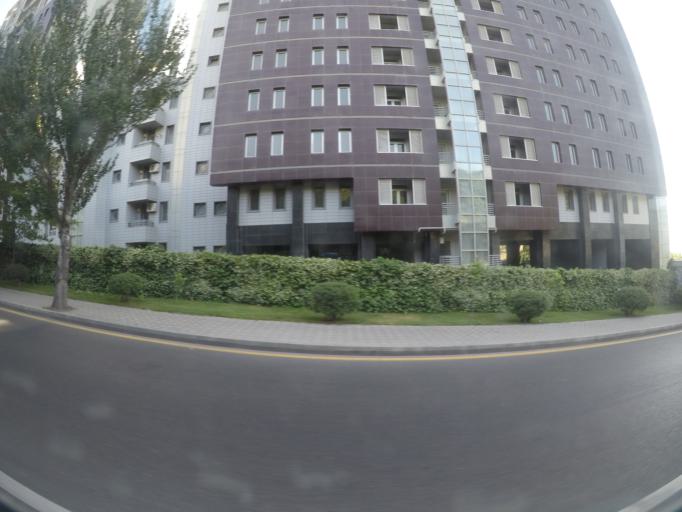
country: AZ
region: Baki
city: Badamdar
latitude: 40.3661
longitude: 49.8252
